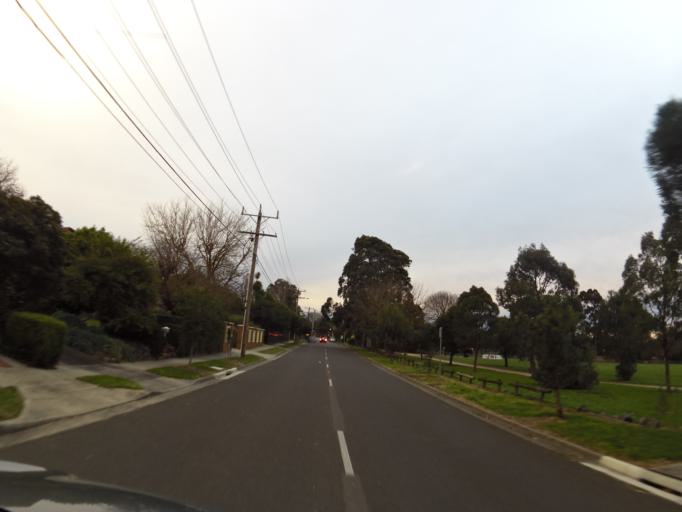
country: AU
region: Victoria
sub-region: Knox
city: Ferntree Gully
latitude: -37.8972
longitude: 145.3018
